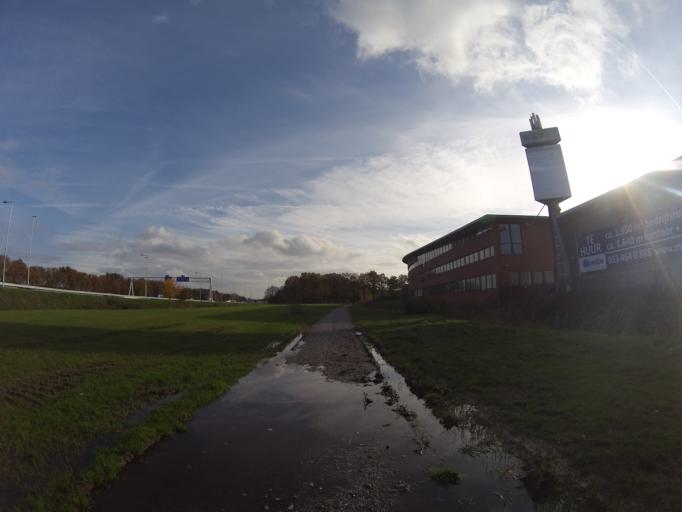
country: NL
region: Utrecht
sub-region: Gemeente Amersfoort
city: Randenbroek
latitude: 52.1796
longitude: 5.4216
